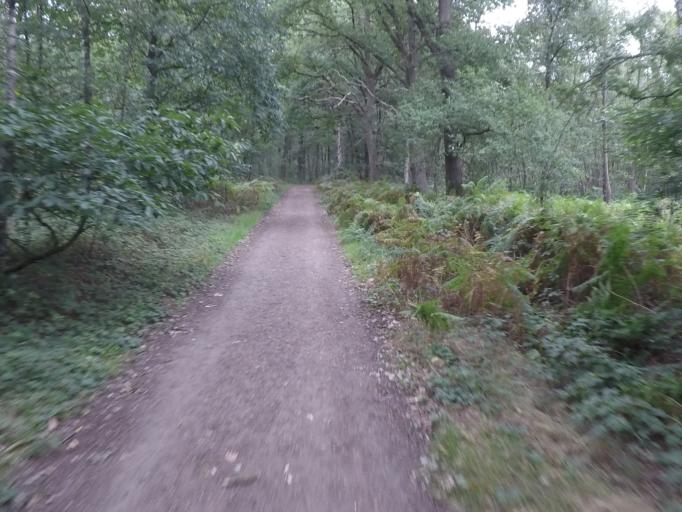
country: BE
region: Flanders
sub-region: Provincie Antwerpen
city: Herentals
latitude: 51.1925
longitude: 4.8618
